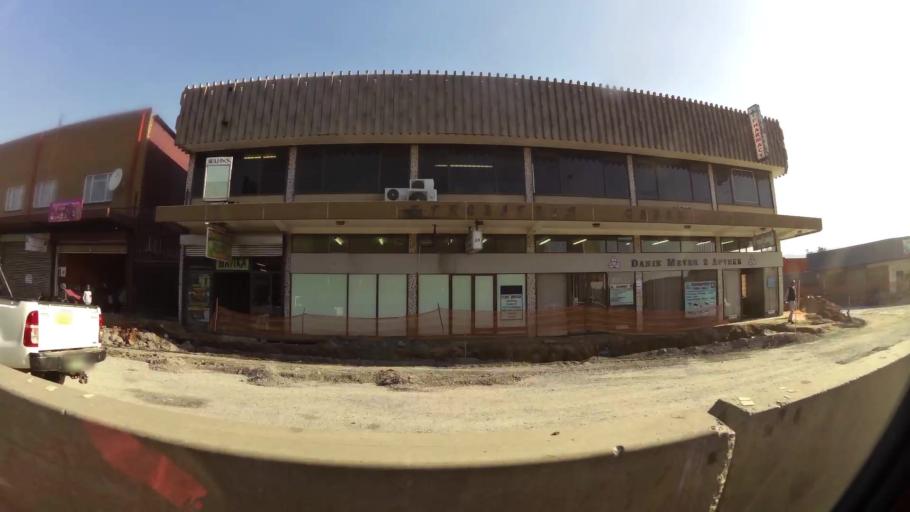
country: ZA
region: North-West
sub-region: Bojanala Platinum District Municipality
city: Rustenburg
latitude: -25.6671
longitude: 27.2377
